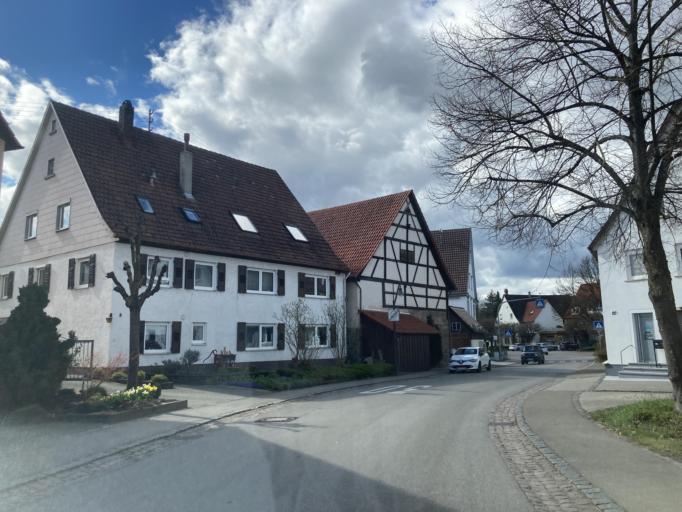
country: DE
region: Baden-Wuerttemberg
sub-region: Tuebingen Region
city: Hirrlingen
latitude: 48.4103
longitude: 8.8892
